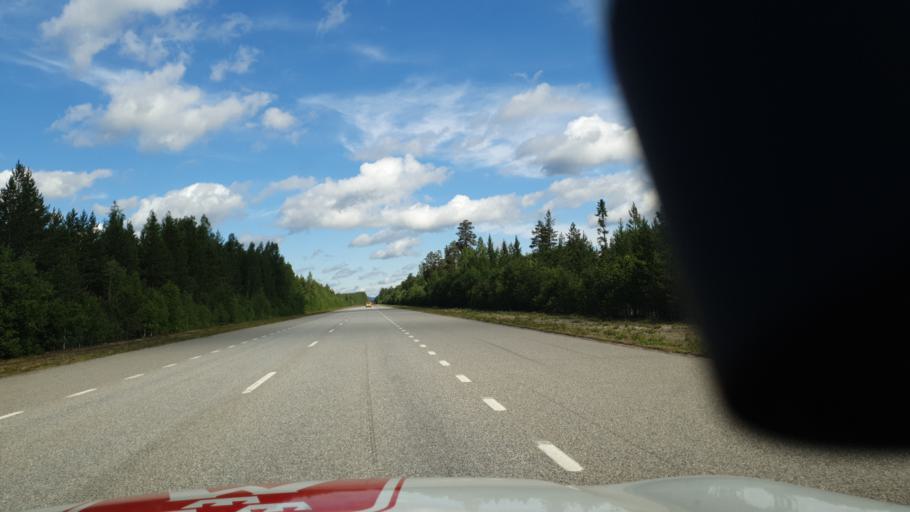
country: SE
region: Vaesterbotten
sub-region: Norsjo Kommun
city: Norsjoe
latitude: 64.5692
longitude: 19.3120
